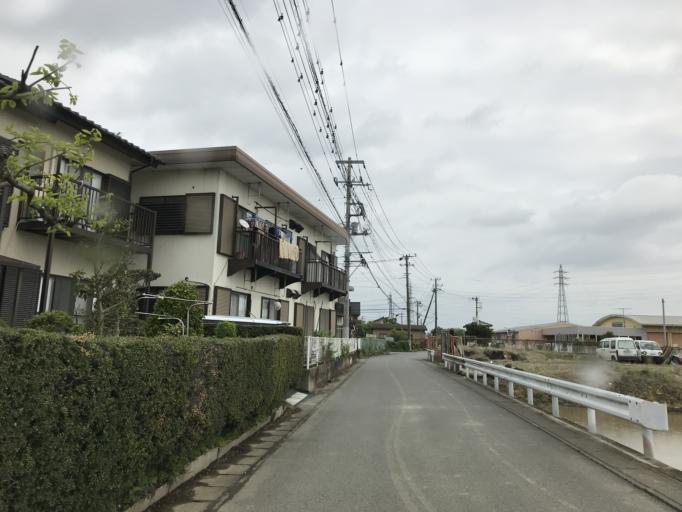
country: JP
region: Ibaraki
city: Mitsukaido
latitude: 36.0111
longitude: 139.9848
